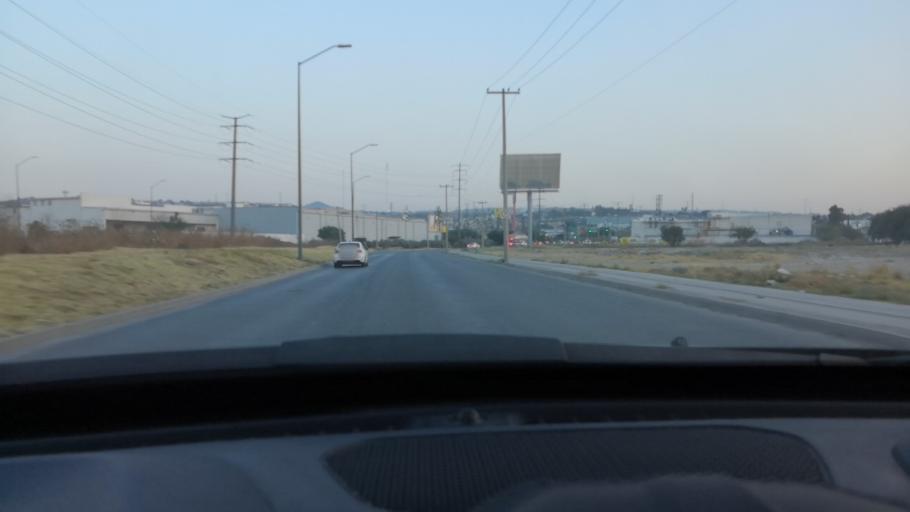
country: MX
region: Guanajuato
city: Leon
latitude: 21.0988
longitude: -101.7080
